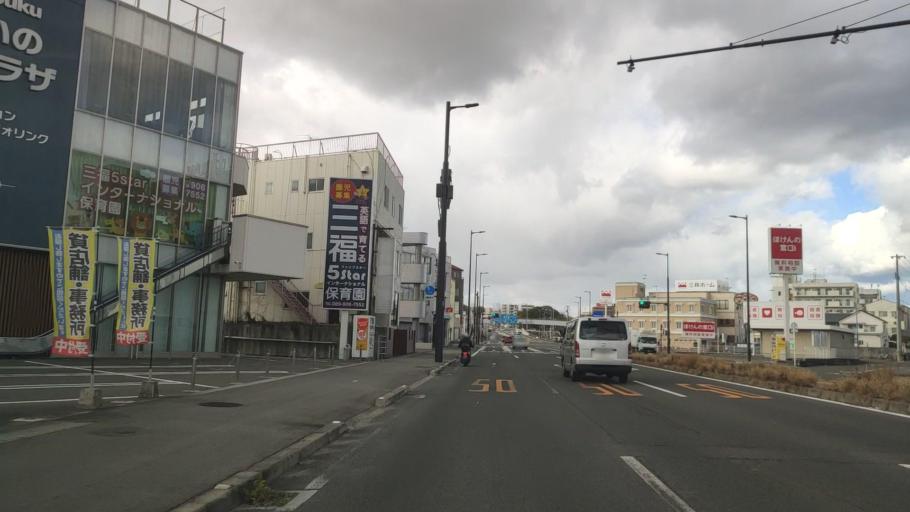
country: JP
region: Ehime
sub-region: Shikoku-chuo Shi
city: Matsuyama
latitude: 33.8319
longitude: 132.7791
